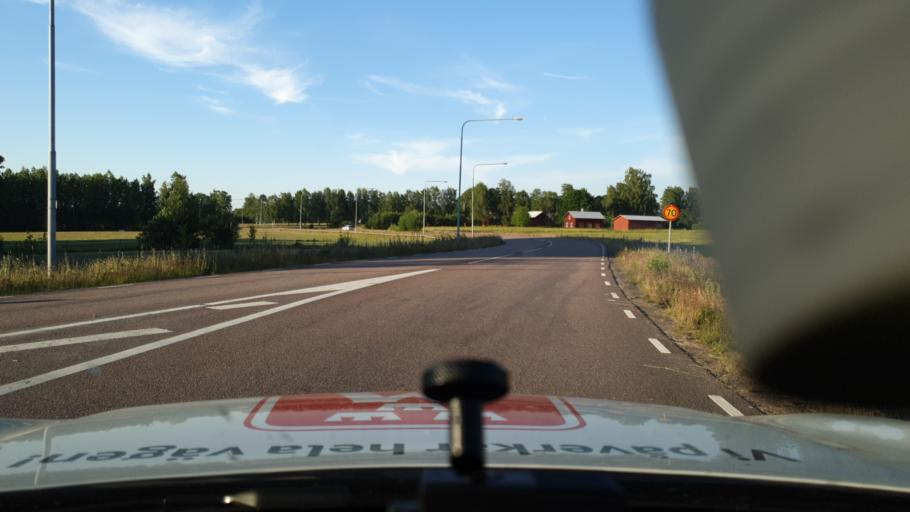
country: SE
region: Vaermland
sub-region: Kils Kommun
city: Kil
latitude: 59.5208
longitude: 13.3052
